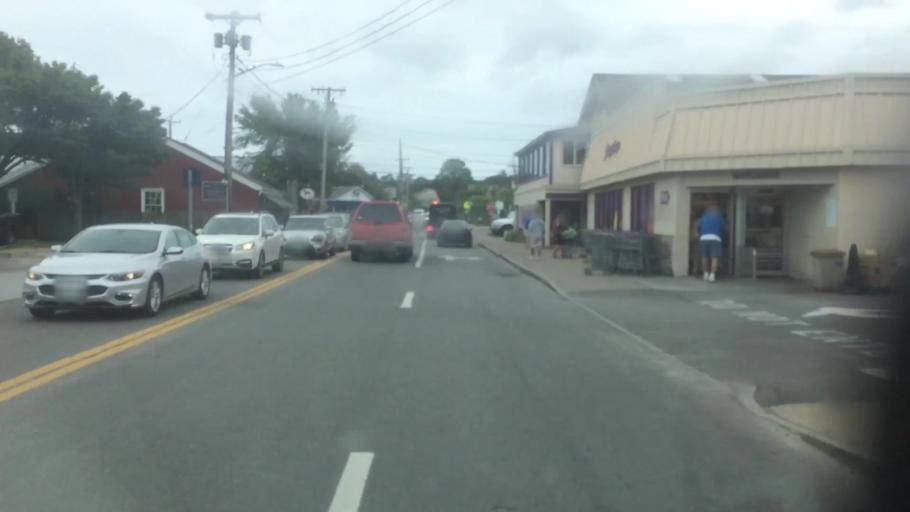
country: US
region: Massachusetts
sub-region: Dukes County
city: Vineyard Haven
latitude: 41.4548
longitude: -70.6013
